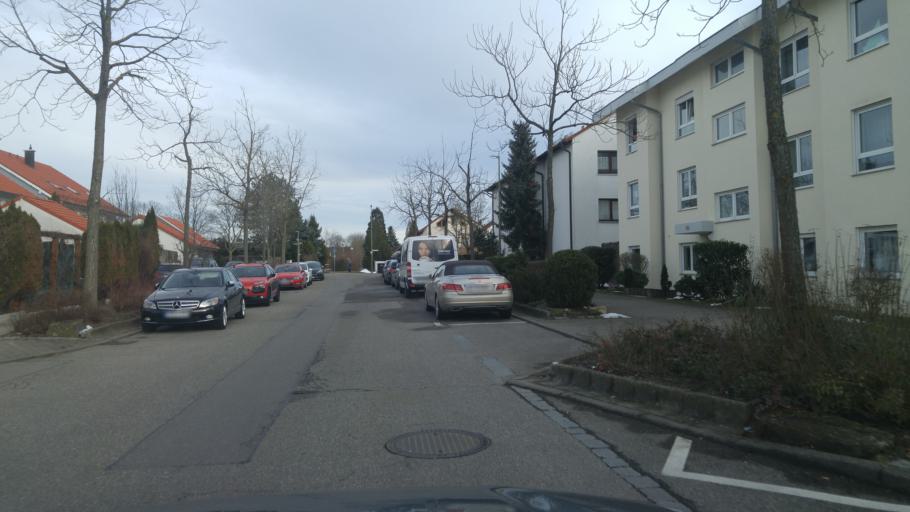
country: DE
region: Baden-Wuerttemberg
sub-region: Regierungsbezirk Stuttgart
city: Leonberg
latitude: 48.7913
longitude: 8.9910
